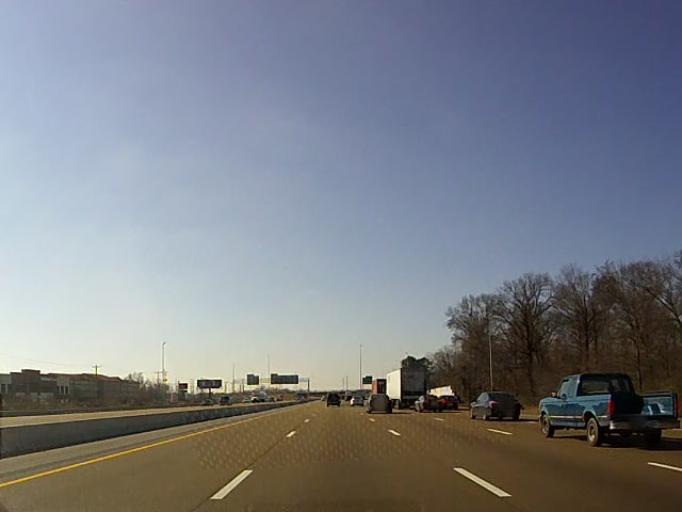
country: US
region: Tennessee
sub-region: Shelby County
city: Germantown
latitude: 35.0801
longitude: -89.9026
